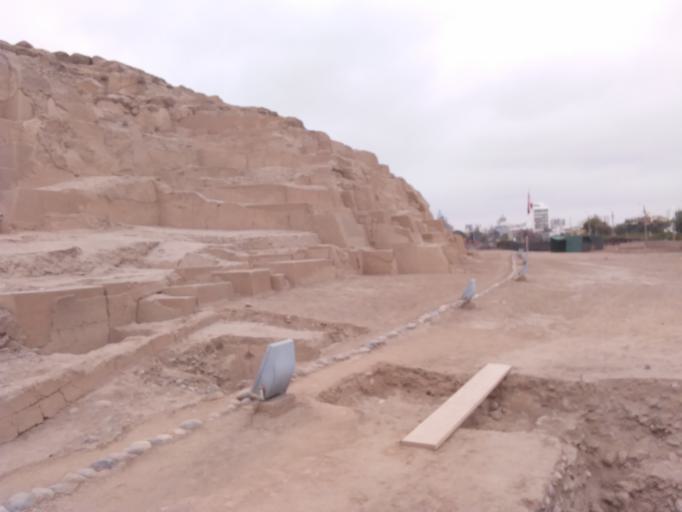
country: PE
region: Lima
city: Lima
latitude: -12.0669
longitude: -77.0646
